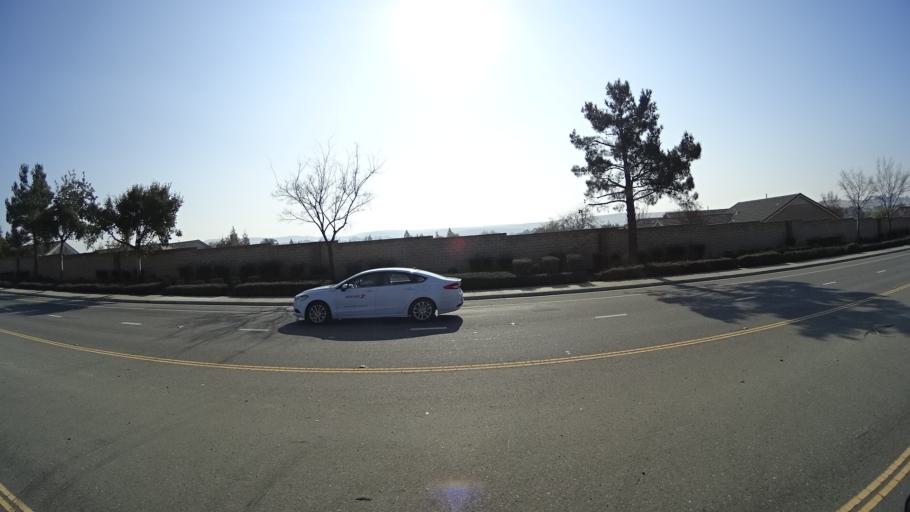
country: US
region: California
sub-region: Kern County
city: Lamont
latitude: 35.4104
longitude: -118.8509
